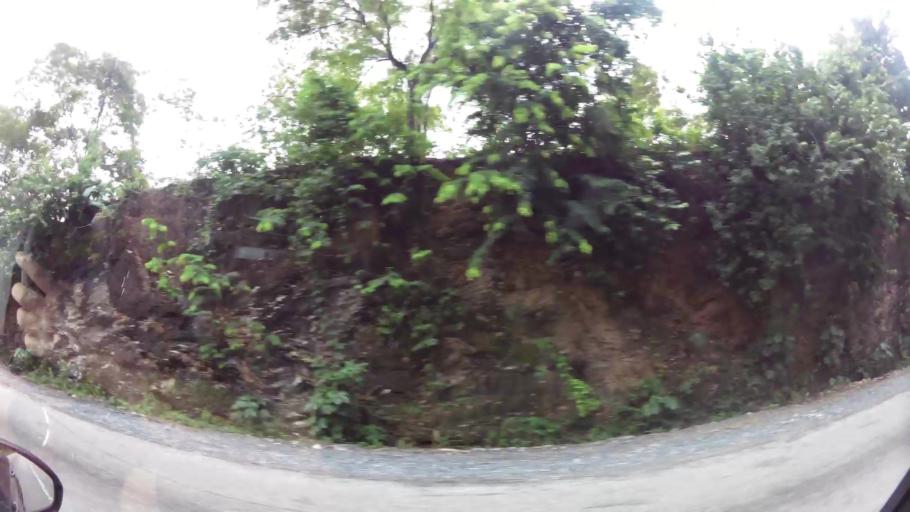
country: TT
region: City of Port of Spain
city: Port-of-Spain
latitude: 10.6742
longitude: -61.5032
